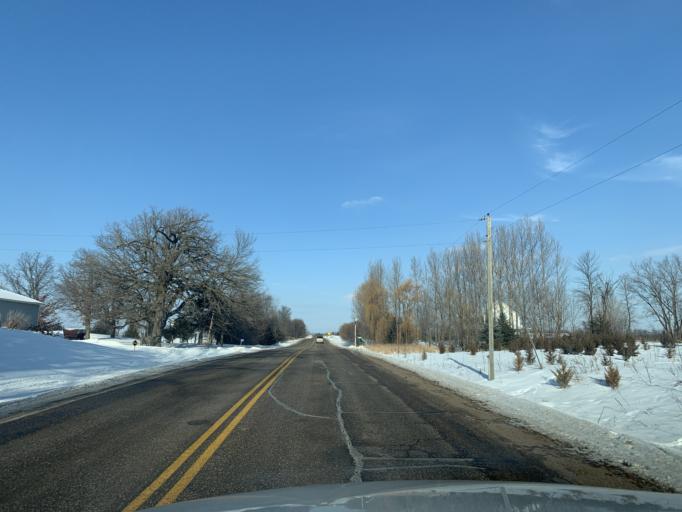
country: US
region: Minnesota
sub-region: Wright County
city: Buffalo
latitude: 45.1981
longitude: -93.8271
